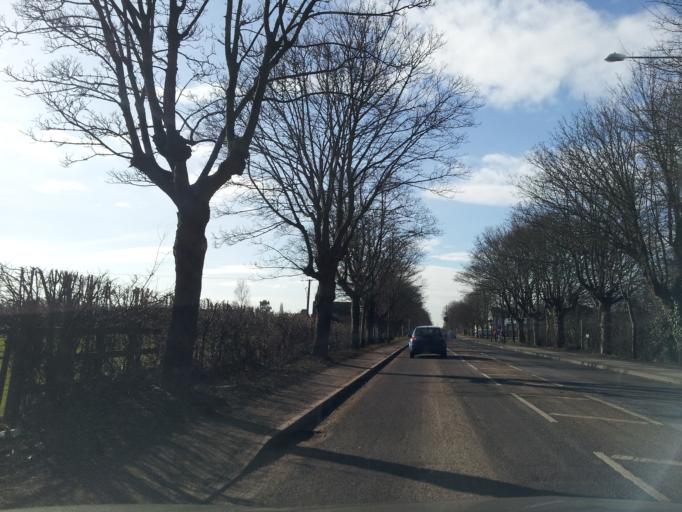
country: GB
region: England
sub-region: Nottinghamshire
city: Newark on Trent
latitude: 53.0693
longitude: -0.8258
